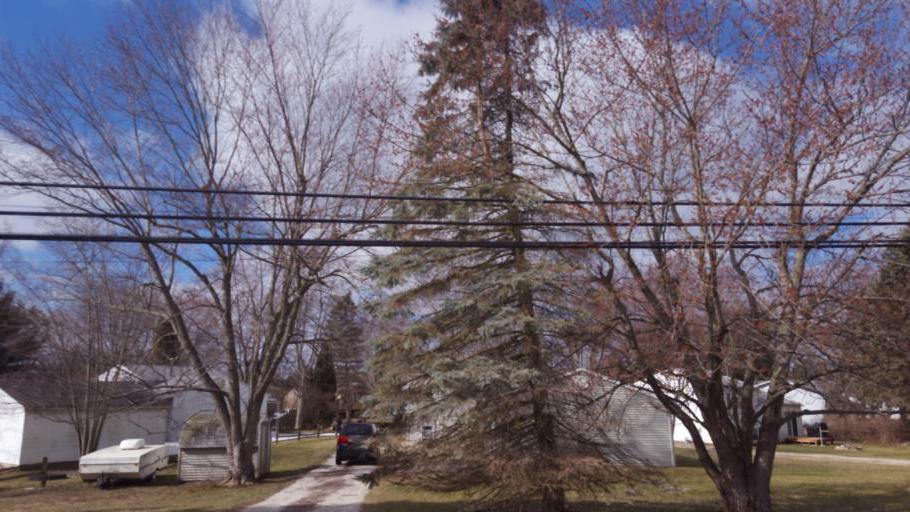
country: US
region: Ohio
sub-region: Richland County
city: Mansfield
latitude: 40.7169
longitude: -82.5121
